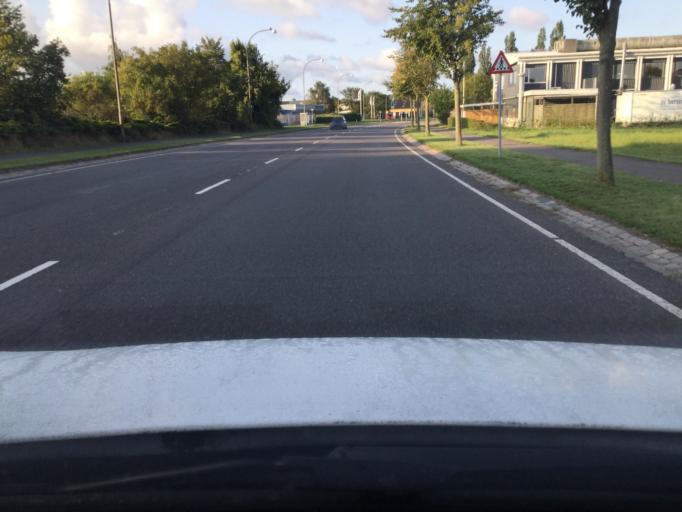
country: DK
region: Zealand
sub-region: Lolland Kommune
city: Nakskov
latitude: 54.8279
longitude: 11.1620
